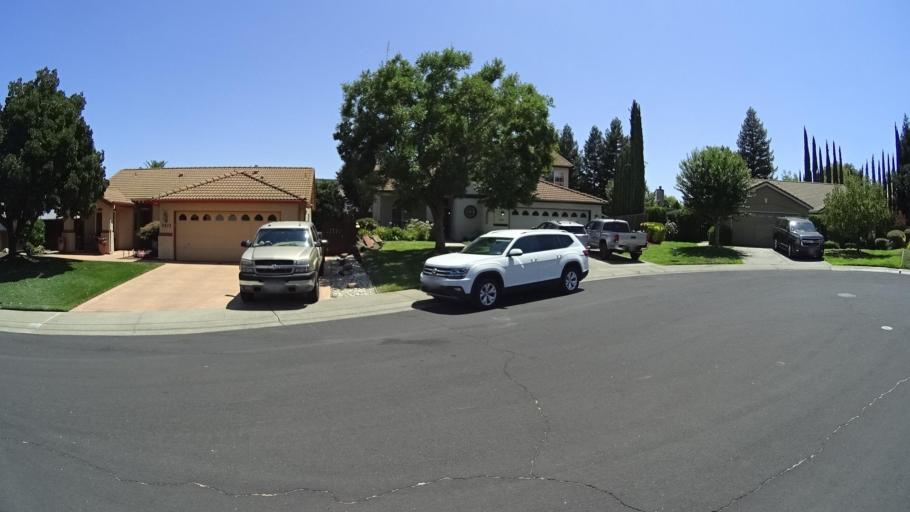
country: US
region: California
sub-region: Placer County
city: Rocklin
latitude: 38.8212
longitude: -121.2671
